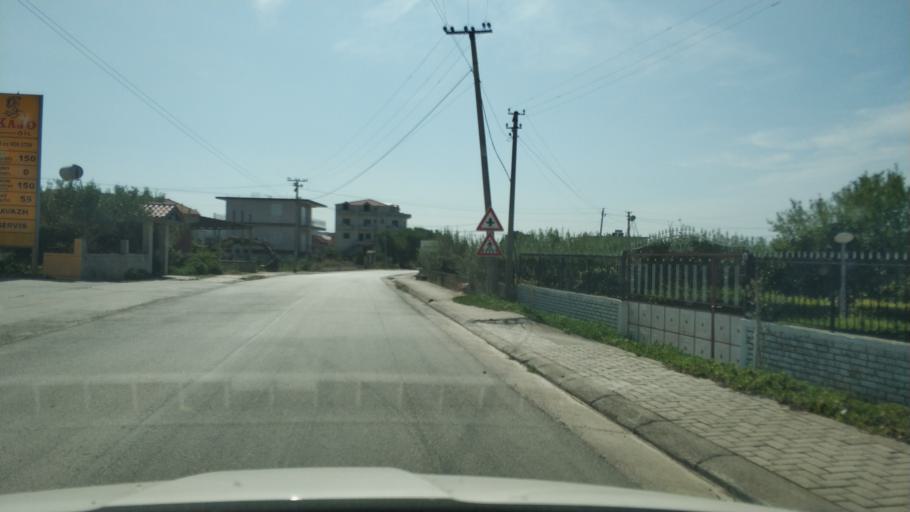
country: AL
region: Fier
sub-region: Rrethi i Lushnjes
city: Divjake
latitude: 40.9784
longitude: 19.5354
